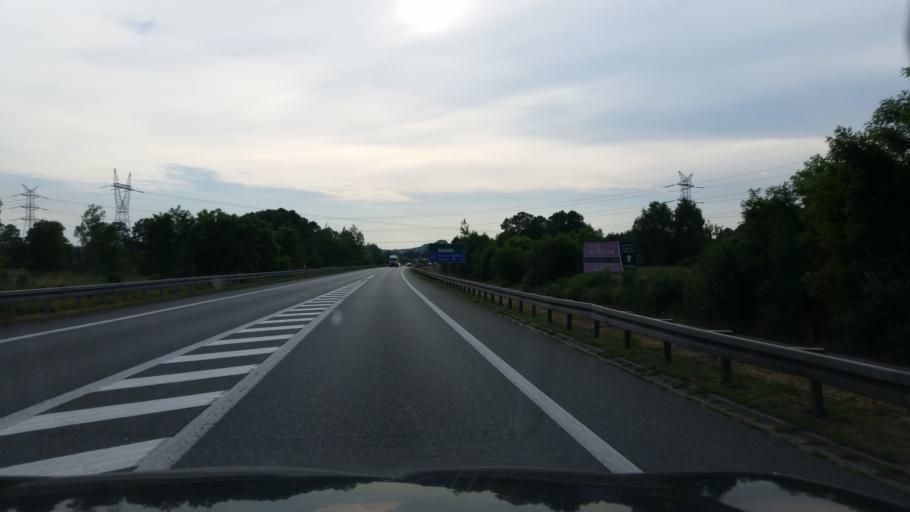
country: PL
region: Silesian Voivodeship
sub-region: Powiat bedzinski
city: Siewierz
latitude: 50.4207
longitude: 19.1949
